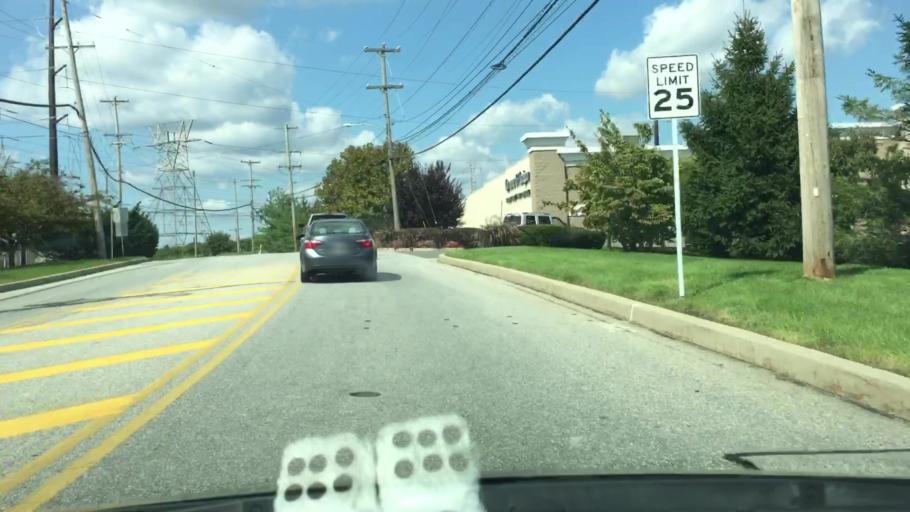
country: US
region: Pennsylvania
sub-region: Montgomery County
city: Plymouth Meeting
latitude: 40.1040
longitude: -75.2967
